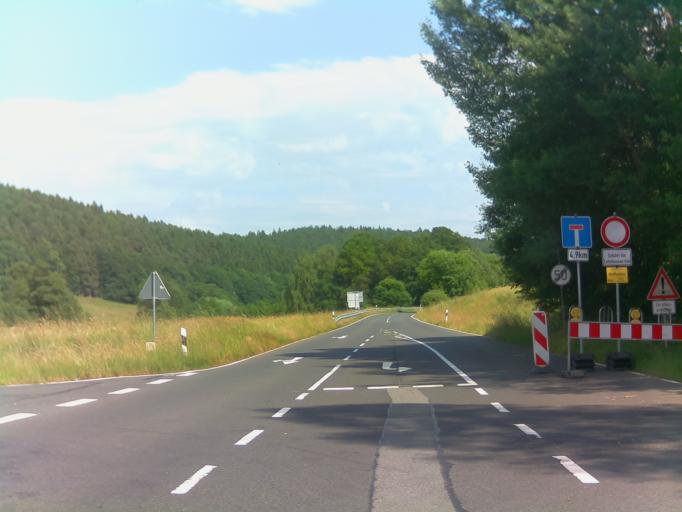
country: DE
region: Hesse
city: Rosenthal
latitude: 50.9930
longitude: 8.9094
